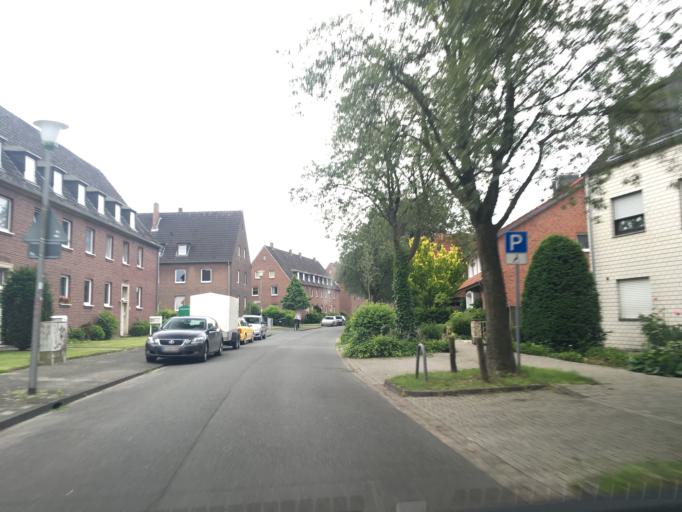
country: DE
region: North Rhine-Westphalia
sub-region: Regierungsbezirk Munster
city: Muenster
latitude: 51.9389
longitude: 7.6170
